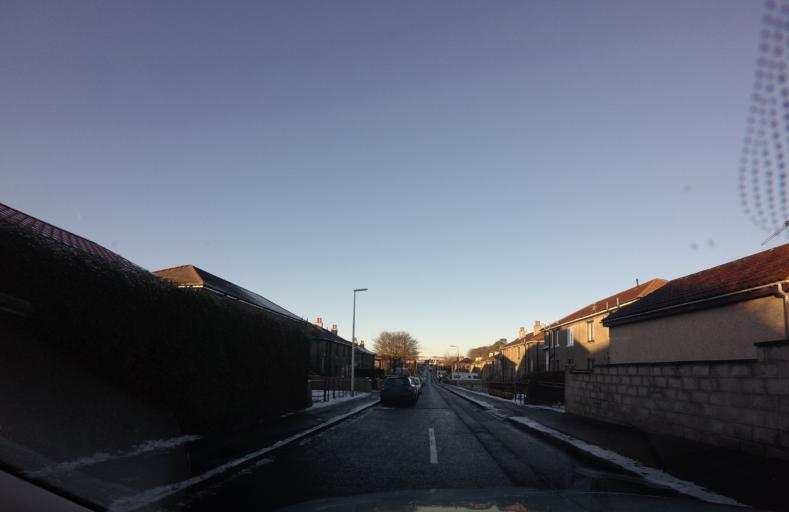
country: GB
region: Scotland
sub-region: Dundee City
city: Dundee
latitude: 56.4751
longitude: -2.9899
